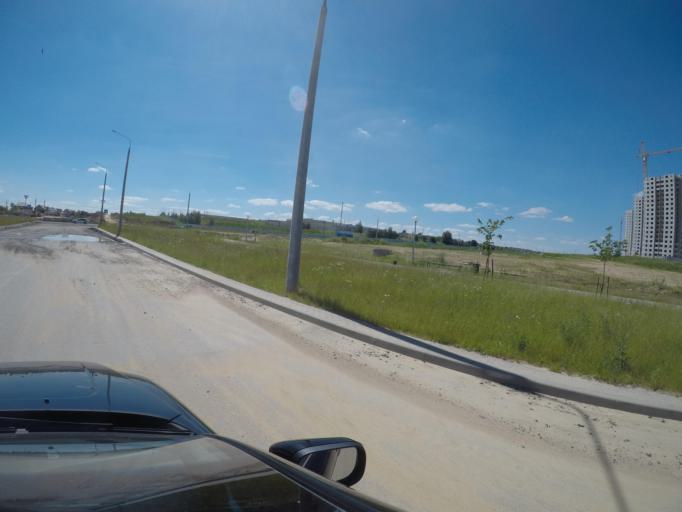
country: BY
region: Grodnenskaya
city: Hrodna
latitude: 53.7215
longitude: 23.8874
